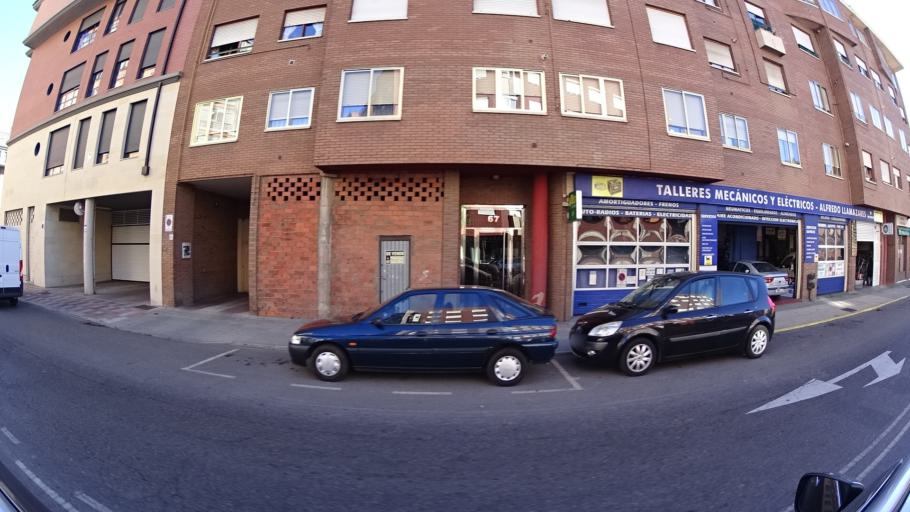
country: ES
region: Castille and Leon
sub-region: Provincia de Leon
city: Leon
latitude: 42.5890
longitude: -5.5620
